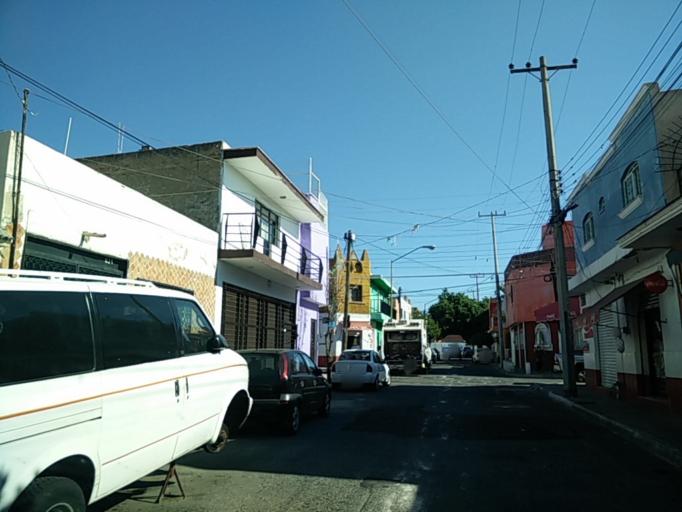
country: MX
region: Jalisco
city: Tlaquepaque
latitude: 20.6631
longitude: -103.3320
